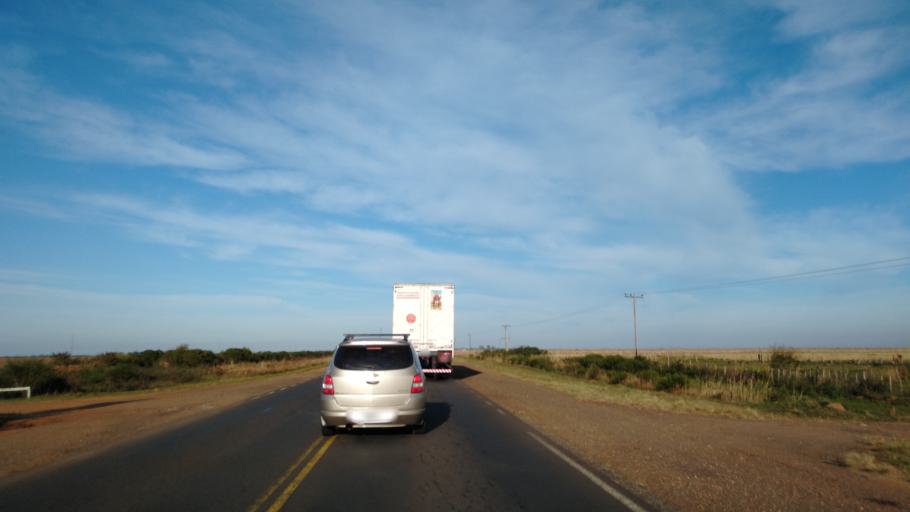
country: AR
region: Corrientes
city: La Cruz
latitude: -29.2095
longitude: -56.7003
